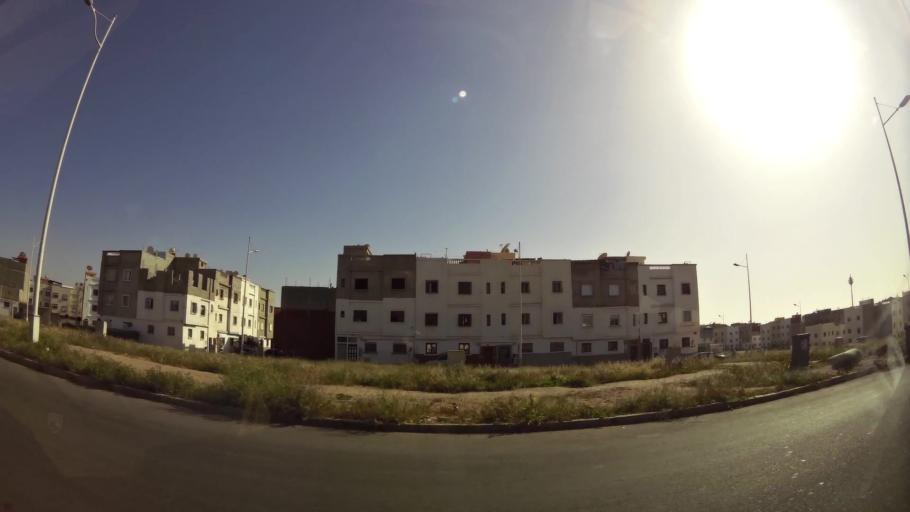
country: MA
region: Oued ed Dahab-Lagouira
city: Dakhla
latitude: 30.4248
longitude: -9.5740
